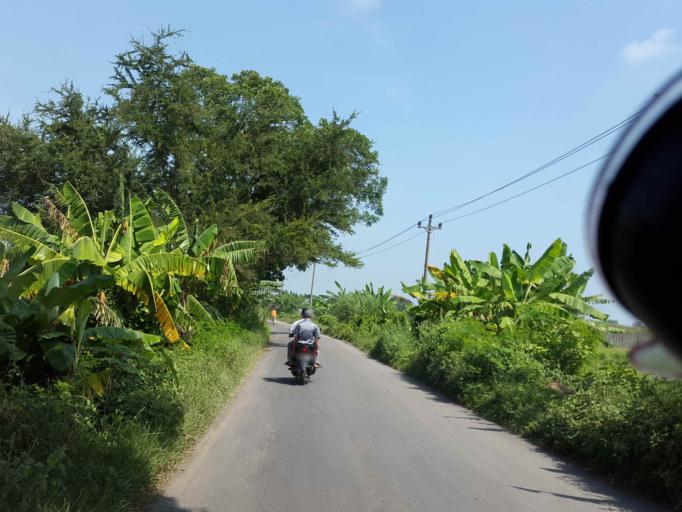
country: ID
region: Central Java
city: Pemalang
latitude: -6.9224
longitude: 109.3342
